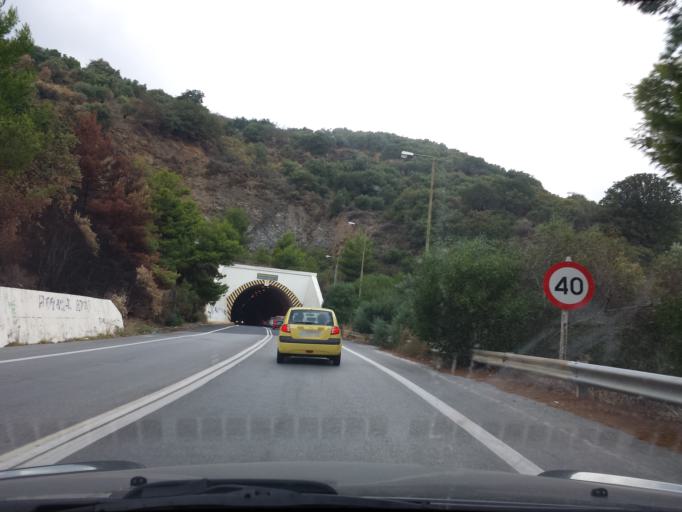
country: GR
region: Crete
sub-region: Nomos Lasithiou
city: Neapoli
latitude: 35.2683
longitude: 25.5769
